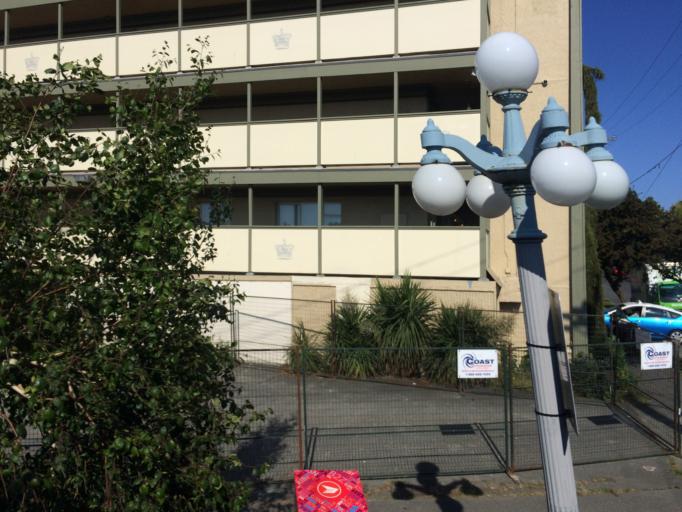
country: CA
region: British Columbia
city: Victoria
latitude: 48.4342
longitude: -123.3645
